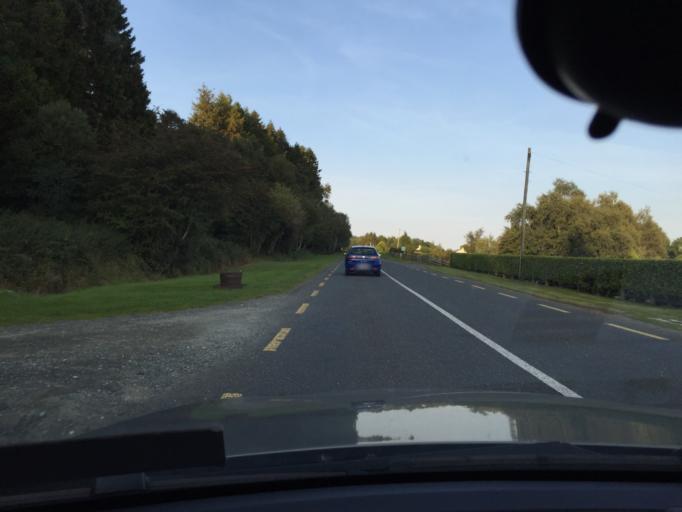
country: IE
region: Leinster
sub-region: Wicklow
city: Rathdrum
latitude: 53.0279
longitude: -6.2646
